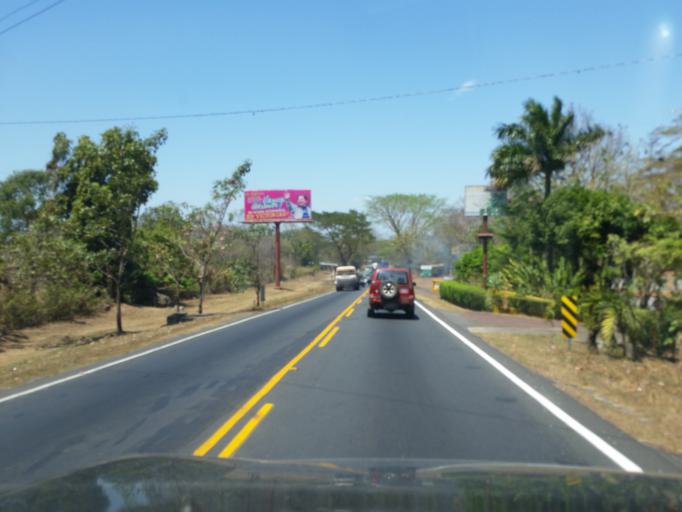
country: NI
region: Masaya
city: Masaya
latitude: 11.9510
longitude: -86.0918
